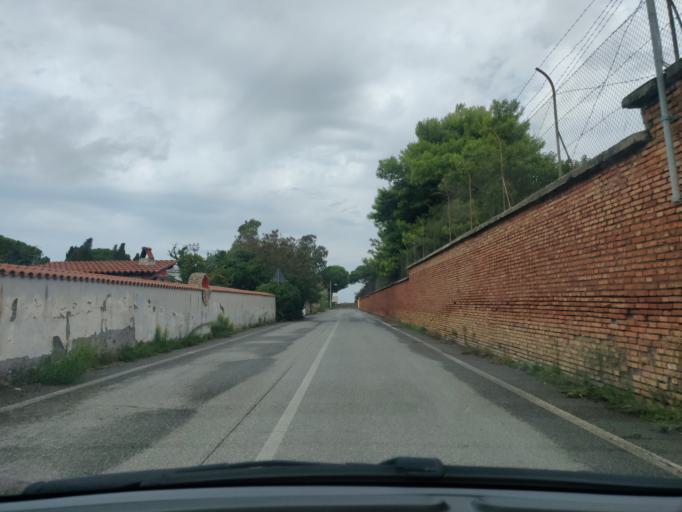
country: IT
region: Latium
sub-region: Citta metropolitana di Roma Capitale
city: Aurelia
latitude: 42.1393
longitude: 11.7871
